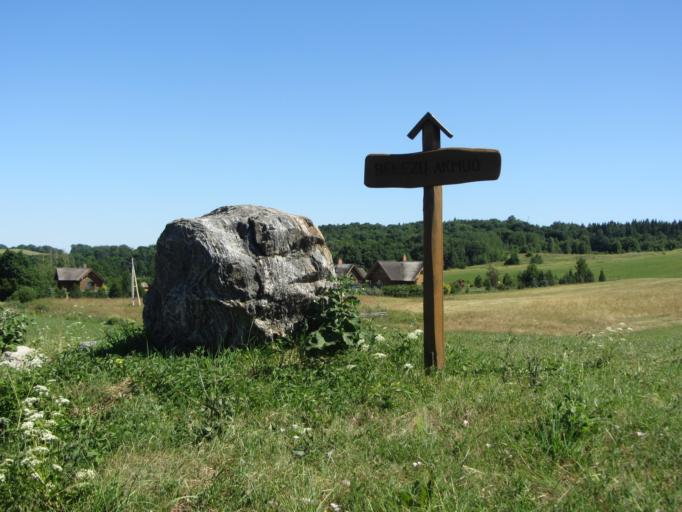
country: LT
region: Vilnius County
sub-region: Vilniaus Rajonas
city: Vievis
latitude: 54.7104
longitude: 24.7360
